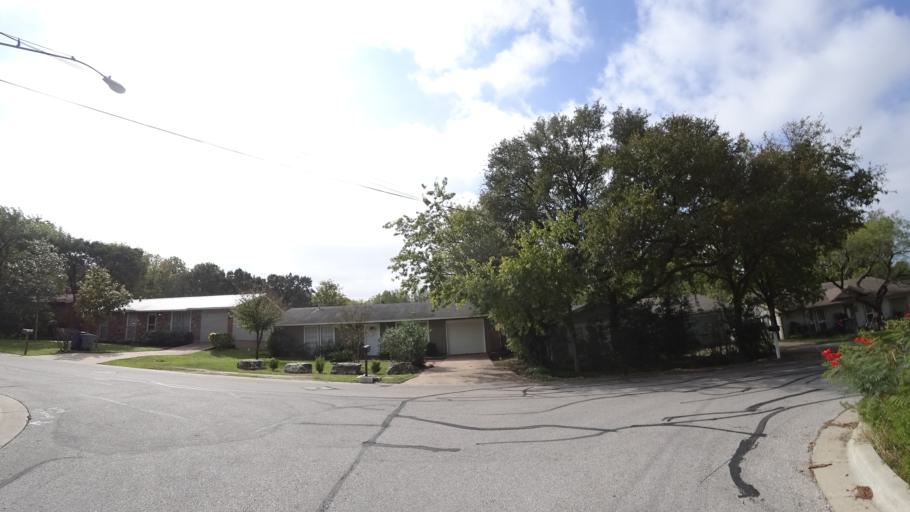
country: US
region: Texas
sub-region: Travis County
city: Shady Hollow
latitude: 30.2020
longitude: -97.8360
